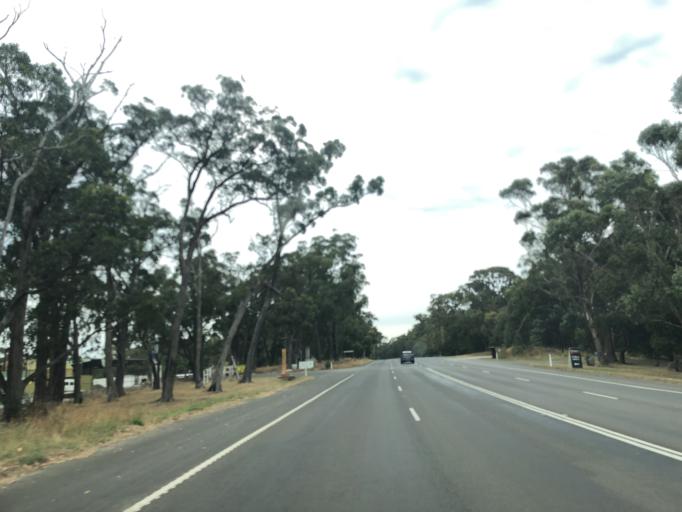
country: AU
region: Victoria
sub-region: Hume
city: Sunbury
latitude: -37.3811
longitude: 144.5276
